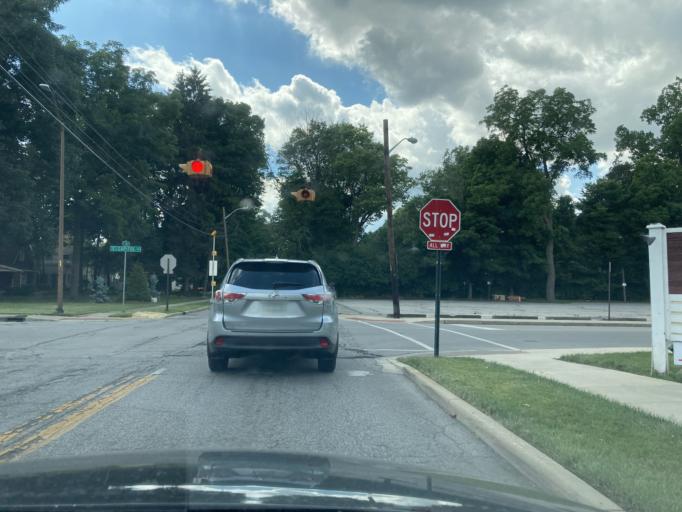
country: US
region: Indiana
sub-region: Marion County
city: Broad Ripple
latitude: 39.8394
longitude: -86.1614
